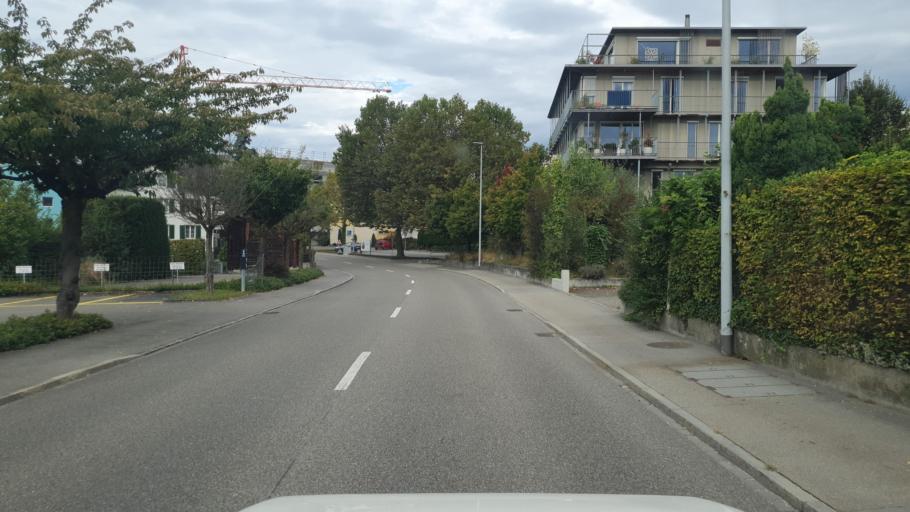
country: CH
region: Aargau
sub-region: Bezirk Bremgarten
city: Wohlen
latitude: 47.3483
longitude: 8.2789
